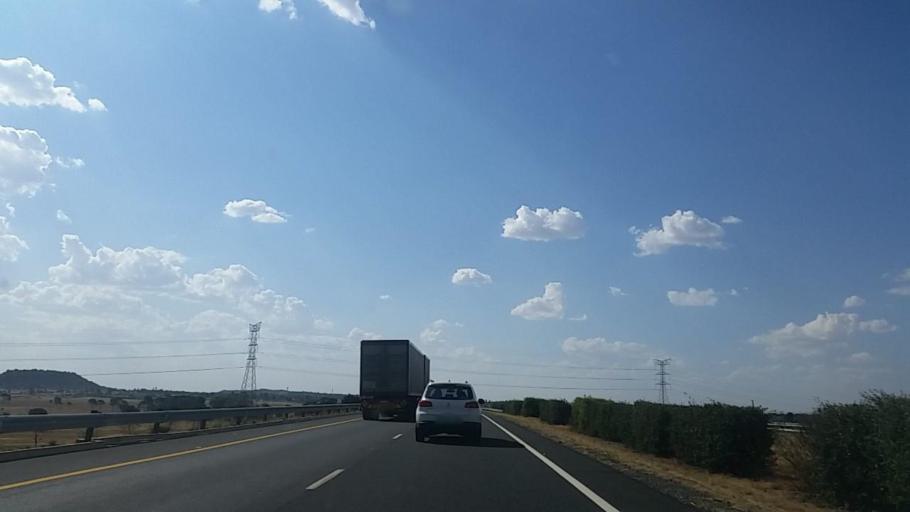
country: ZA
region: Orange Free State
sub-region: Mangaung Metropolitan Municipality
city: Bloemfontein
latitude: -29.1821
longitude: 26.1908
